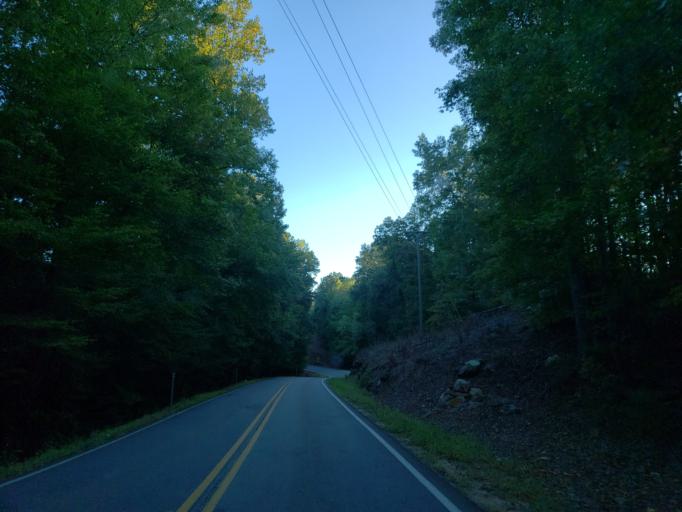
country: US
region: Georgia
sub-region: Bartow County
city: Rydal
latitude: 34.3560
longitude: -84.5801
